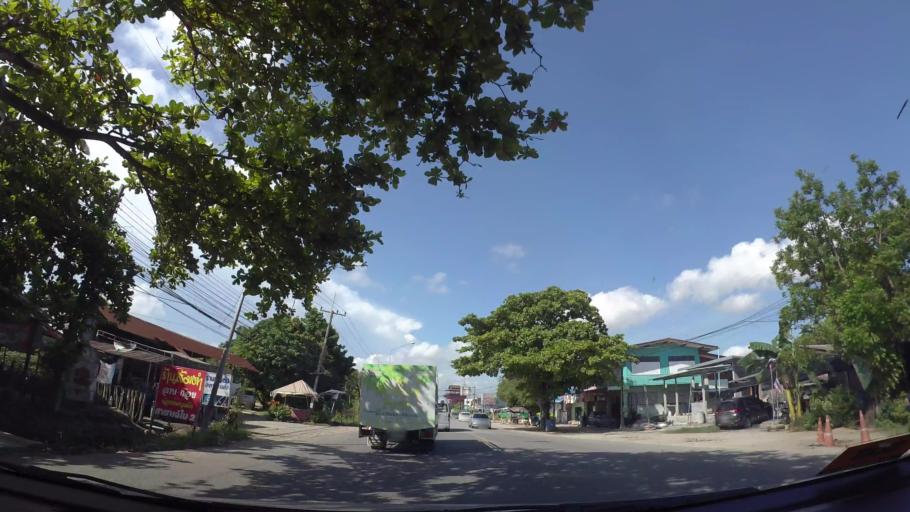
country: TH
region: Rayong
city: Rayong
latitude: 12.6792
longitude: 101.2948
